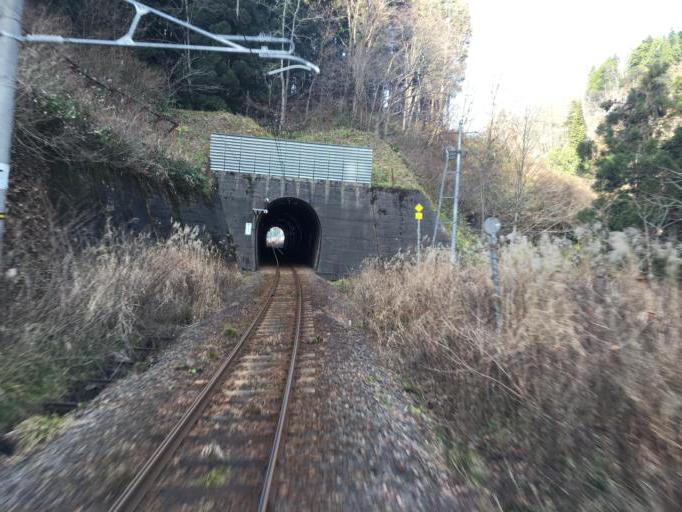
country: JP
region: Akita
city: Yuzawa
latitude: 38.9846
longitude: 140.3625
